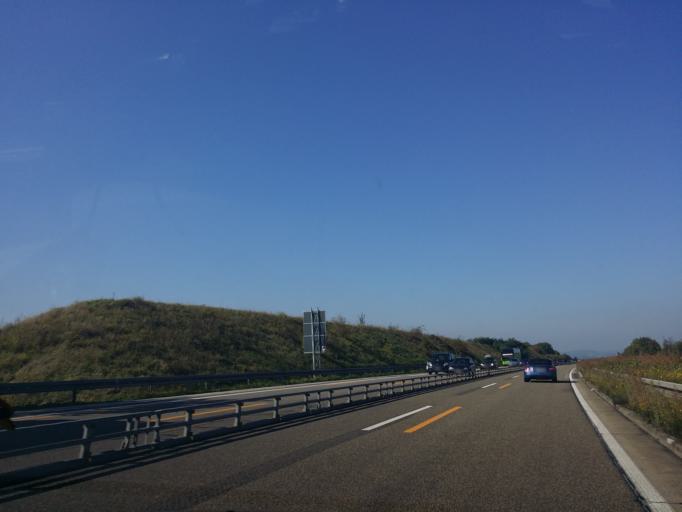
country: DE
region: Hesse
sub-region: Regierungsbezirk Giessen
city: Villmar
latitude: 50.3421
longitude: 8.1769
